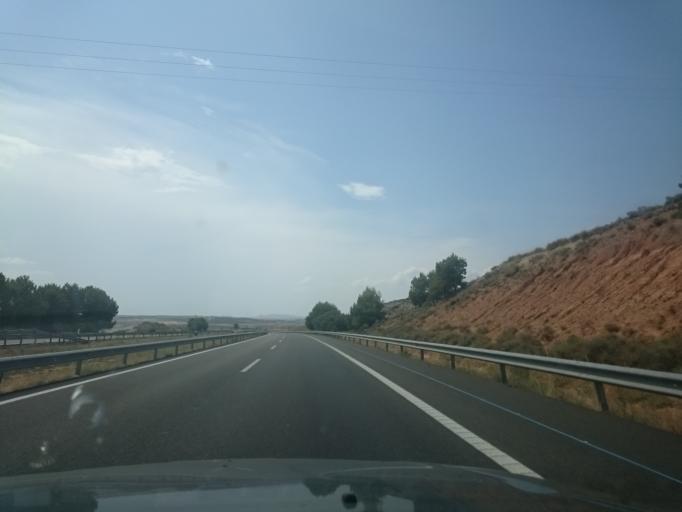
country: ES
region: Aragon
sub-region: Provincia de Huesca
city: Penalba
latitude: 41.5125
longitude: -0.0202
